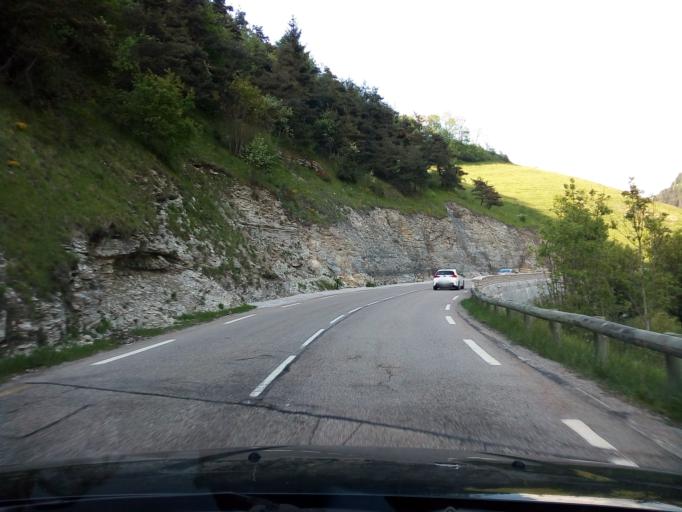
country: FR
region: Rhone-Alpes
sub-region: Departement de l'Isere
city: Lans-en-Vercors
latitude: 45.1733
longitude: 5.6149
